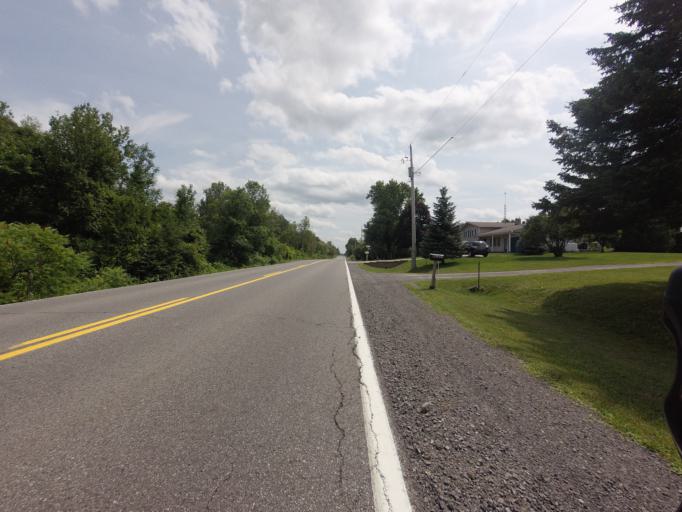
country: CA
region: Ontario
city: Ottawa
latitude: 45.2304
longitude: -75.6087
